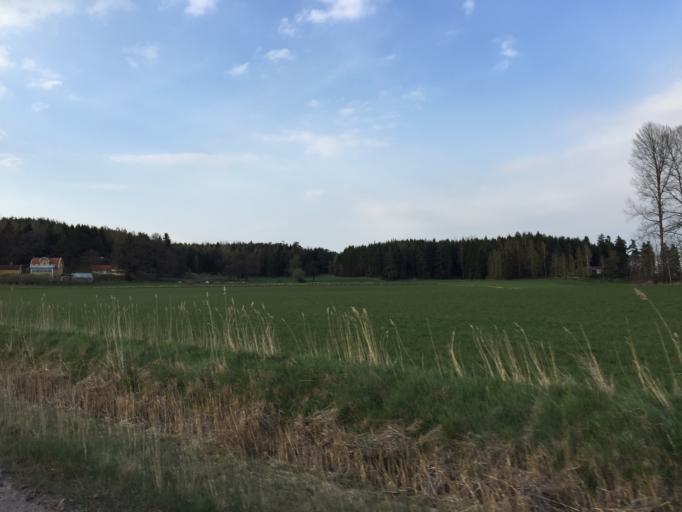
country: SE
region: Soedermanland
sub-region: Trosa Kommun
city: Vagnharad
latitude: 58.9914
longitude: 17.6180
